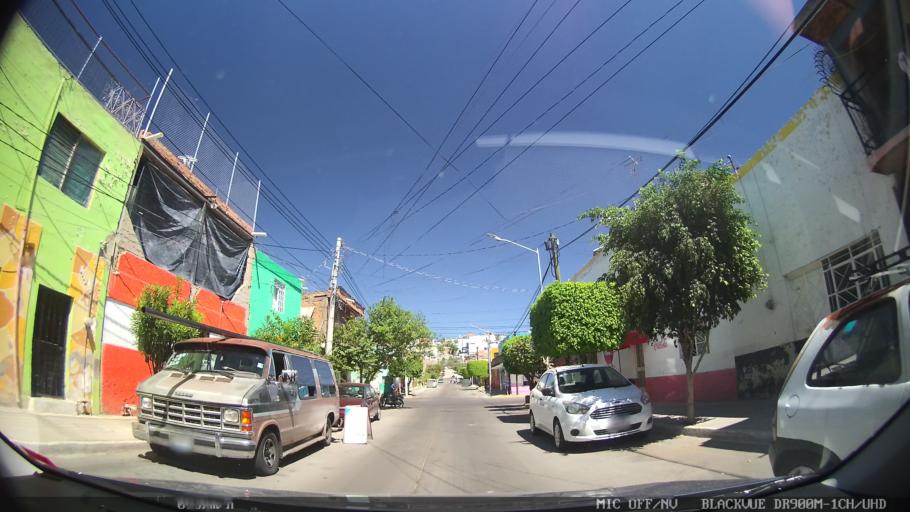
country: MX
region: Jalisco
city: Tlaquepaque
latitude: 20.6879
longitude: -103.2844
